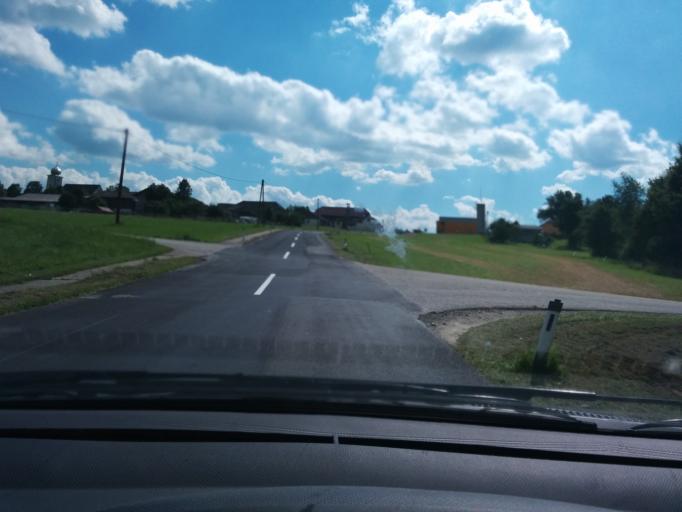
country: AT
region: Upper Austria
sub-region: Politischer Bezirk Rohrbach
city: Ulrichsberg
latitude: 48.6976
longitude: 13.8841
